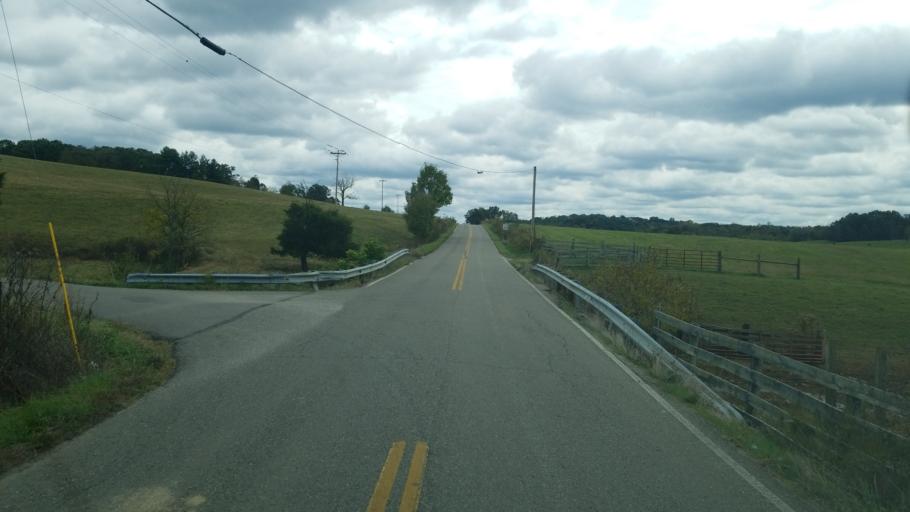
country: US
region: Ohio
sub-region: Jackson County
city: Jackson
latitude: 39.1382
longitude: -82.6502
